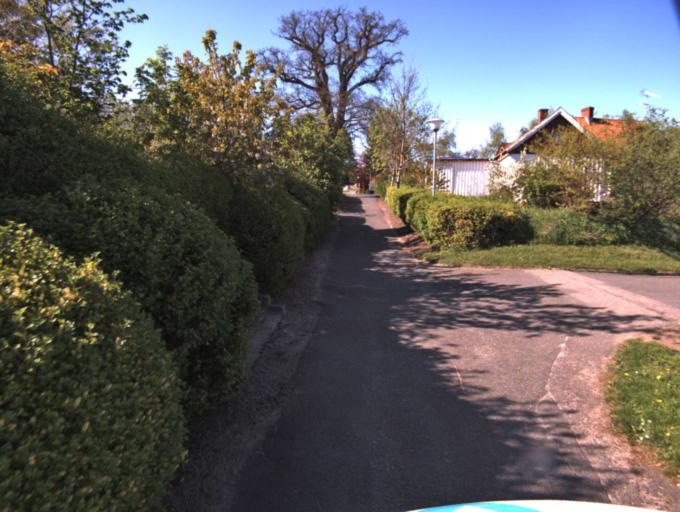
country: SE
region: Skane
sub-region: Kristianstads Kommun
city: Degeberga
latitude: 55.8384
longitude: 14.0939
